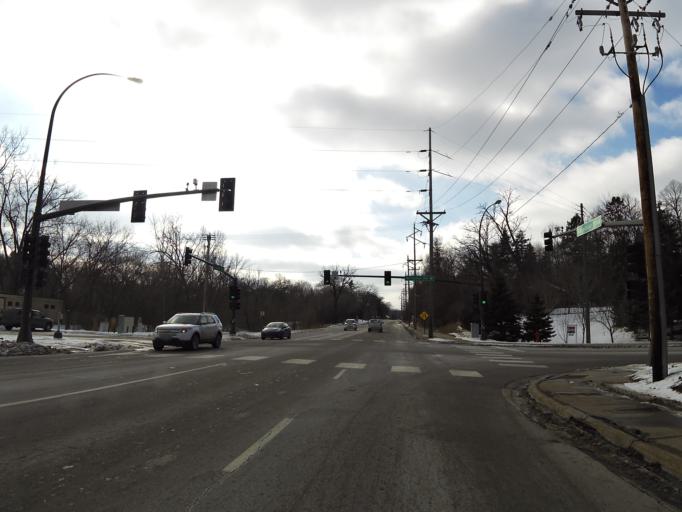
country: US
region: Minnesota
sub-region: Hennepin County
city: Hopkins
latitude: 44.9036
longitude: -93.4674
